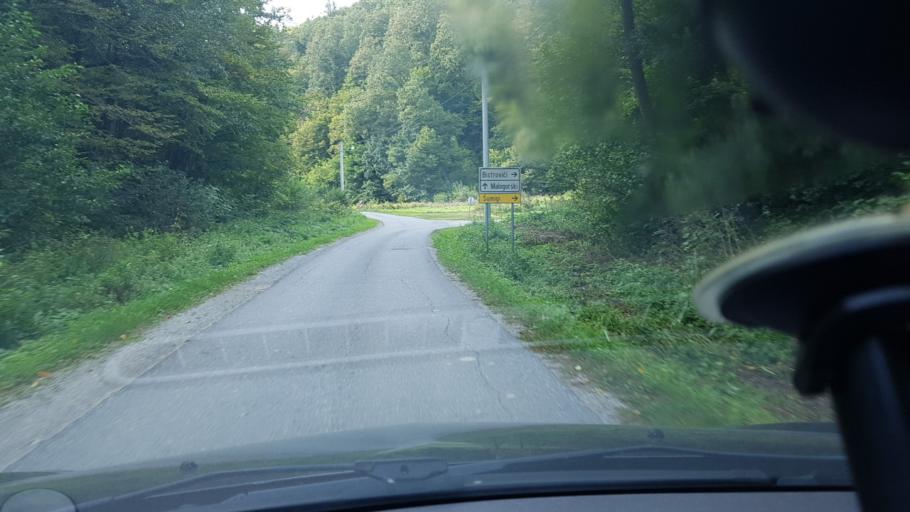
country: HR
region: Krapinsko-Zagorska
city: Mihovljan
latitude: 46.1864
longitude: 15.9757
